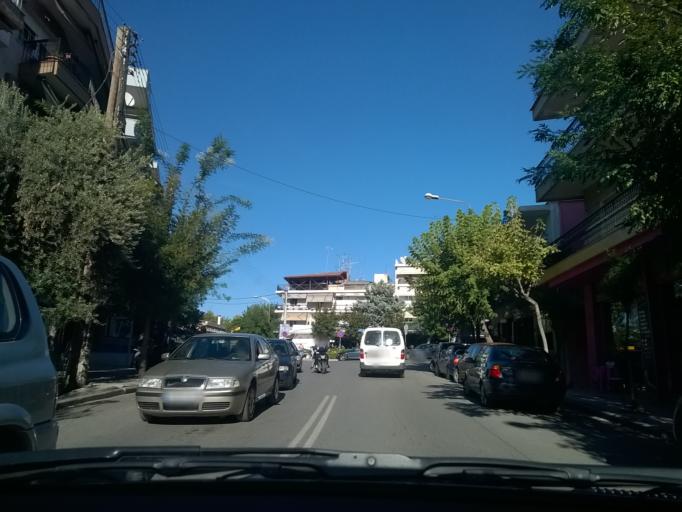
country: GR
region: Central Macedonia
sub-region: Nomos Thessalonikis
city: Polichni
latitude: 40.6584
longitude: 22.9424
